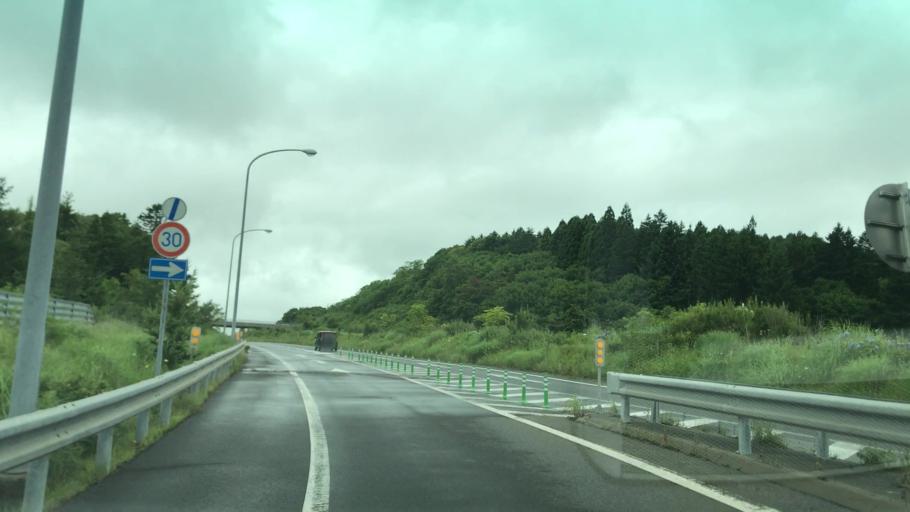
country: JP
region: Hokkaido
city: Muroran
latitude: 42.3848
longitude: 140.9872
